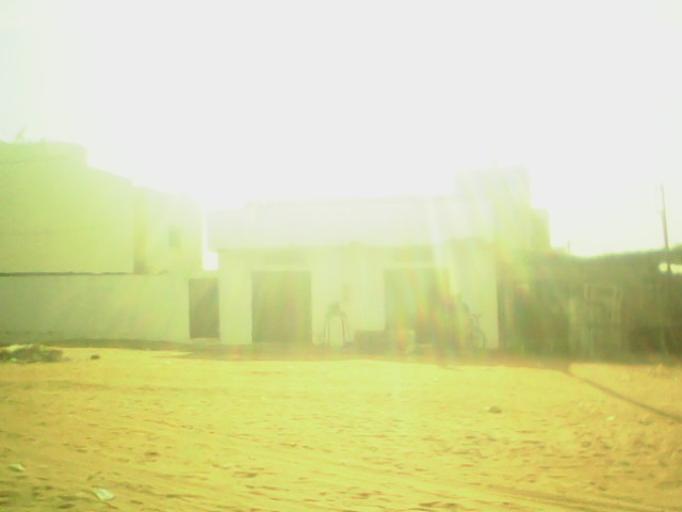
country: SN
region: Diourbel
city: Touba
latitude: 14.8740
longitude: -15.9001
